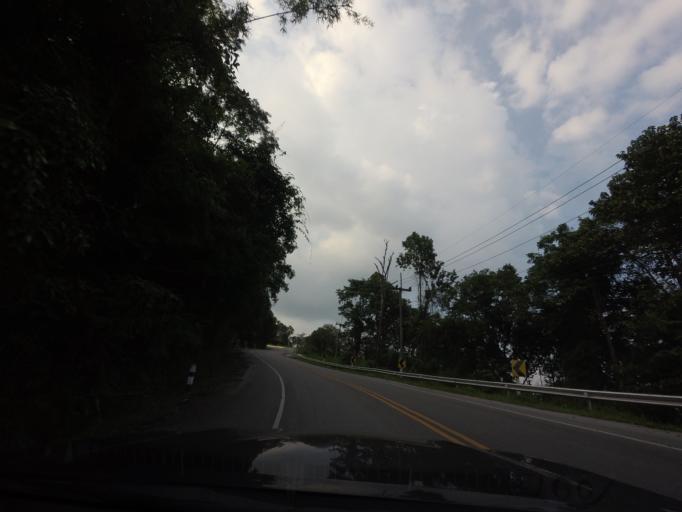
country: TH
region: Loei
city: Dan Sai
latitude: 17.3200
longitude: 101.1238
